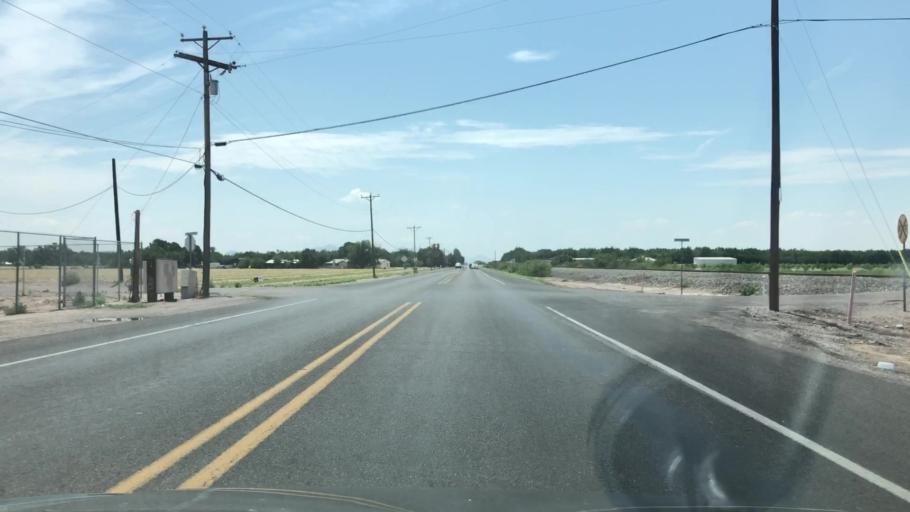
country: US
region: New Mexico
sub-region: Dona Ana County
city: Mesquite
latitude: 32.2091
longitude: -106.7247
